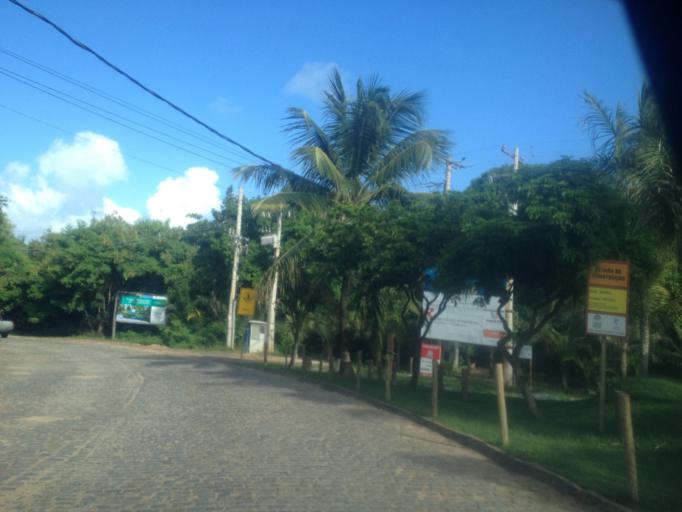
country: BR
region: Bahia
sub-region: Mata De Sao Joao
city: Mata de Sao Joao
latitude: -12.5766
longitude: -38.0169
